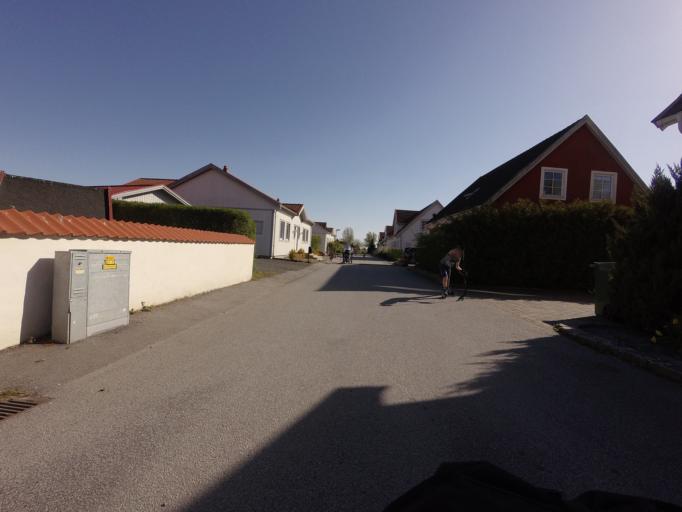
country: SE
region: Skane
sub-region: Landskrona
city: Asmundtorp
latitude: 55.8549
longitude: 12.9066
